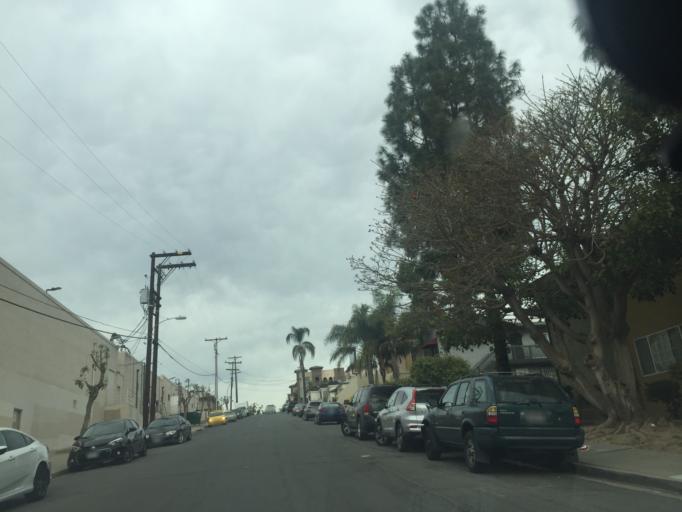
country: US
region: California
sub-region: San Diego County
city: Lemon Grove
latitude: 32.7559
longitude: -117.0826
